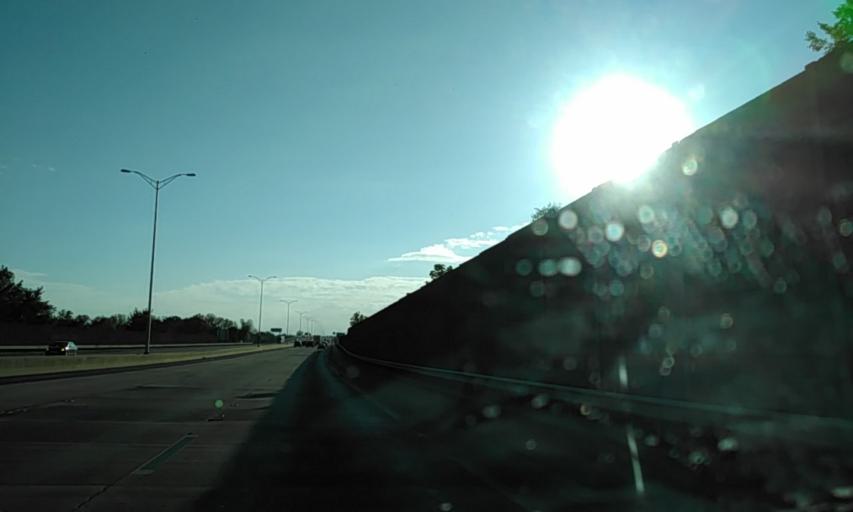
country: US
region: Illinois
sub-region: Saint Clair County
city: Centreville
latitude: 38.5762
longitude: -90.1164
